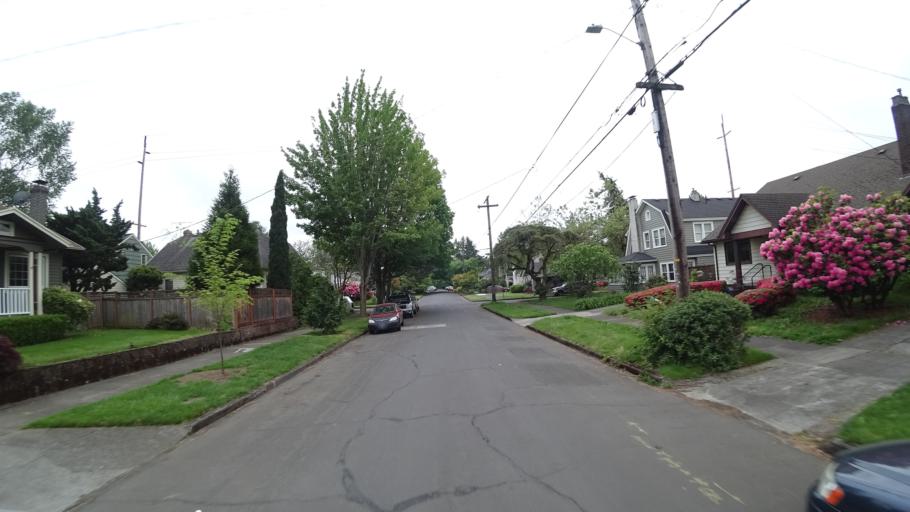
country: US
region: Oregon
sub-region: Multnomah County
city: Portland
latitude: 45.5440
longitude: -122.6277
